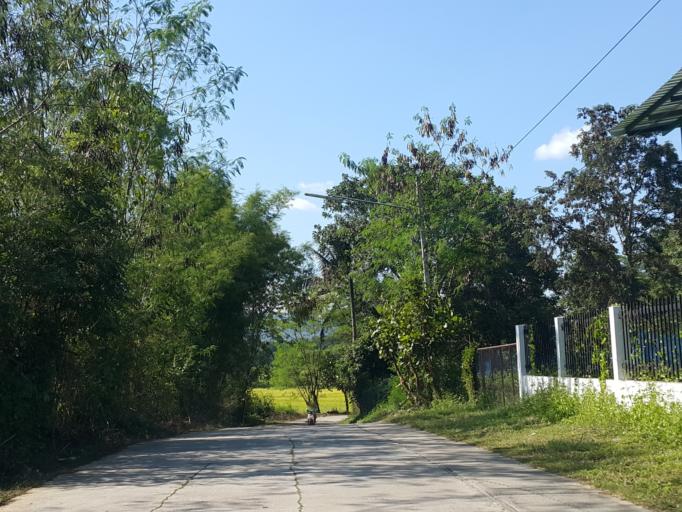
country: TH
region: Chiang Mai
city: San Sai
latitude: 18.9279
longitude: 98.9214
